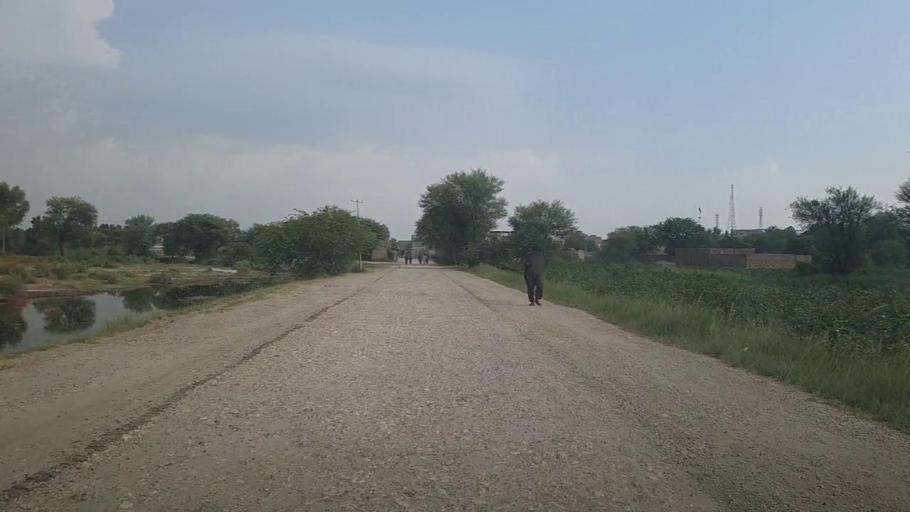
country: PK
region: Sindh
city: Mirpur Mathelo
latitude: 27.9201
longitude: 69.5206
